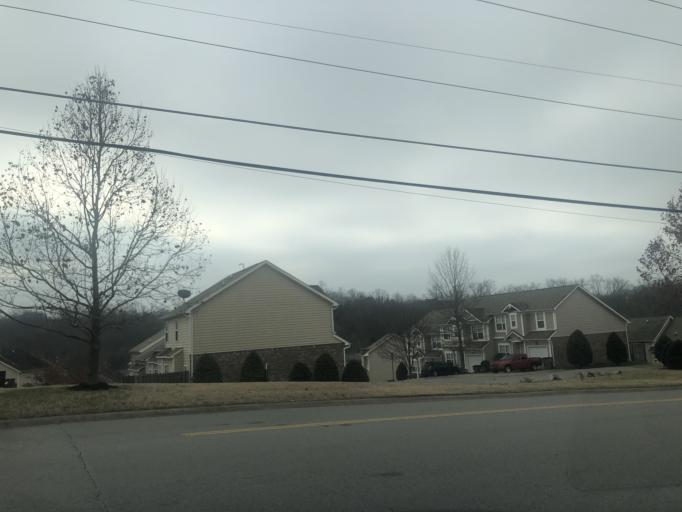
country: US
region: Tennessee
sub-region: Rutherford County
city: La Vergne
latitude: 36.0652
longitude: -86.6458
